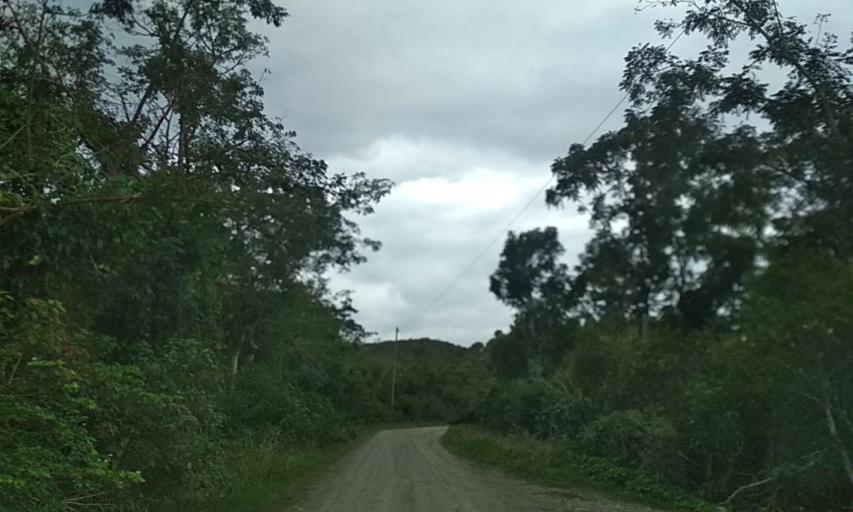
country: MX
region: Veracruz
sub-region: Papantla
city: Polutla
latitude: 20.5134
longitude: -97.2969
